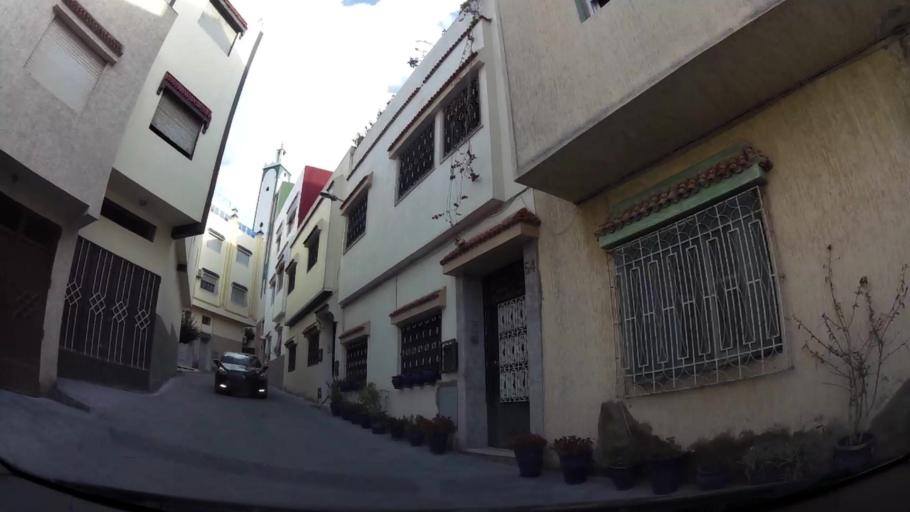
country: MA
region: Tanger-Tetouan
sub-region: Tanger-Assilah
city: Tangier
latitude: 35.7619
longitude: -5.8334
